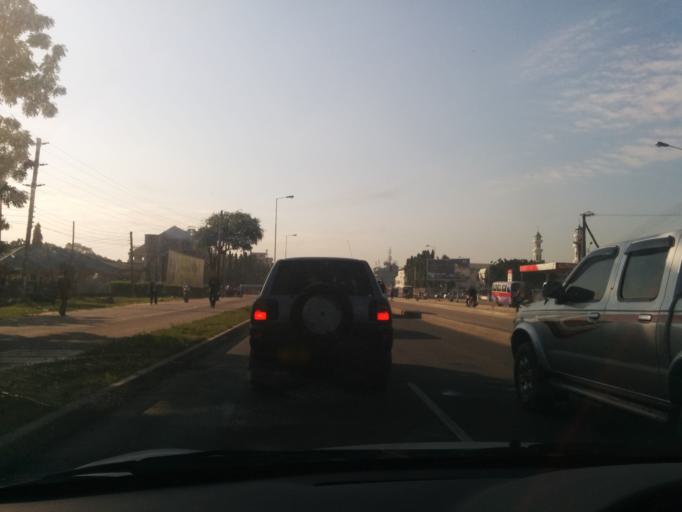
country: TZ
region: Dar es Salaam
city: Magomeni
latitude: -6.8069
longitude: 39.2565
